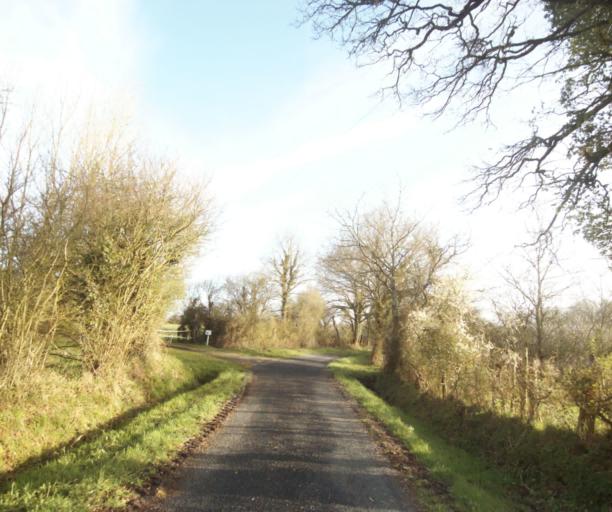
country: FR
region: Pays de la Loire
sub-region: Departement de la Loire-Atlantique
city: Malville
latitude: 47.3868
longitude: -1.8982
